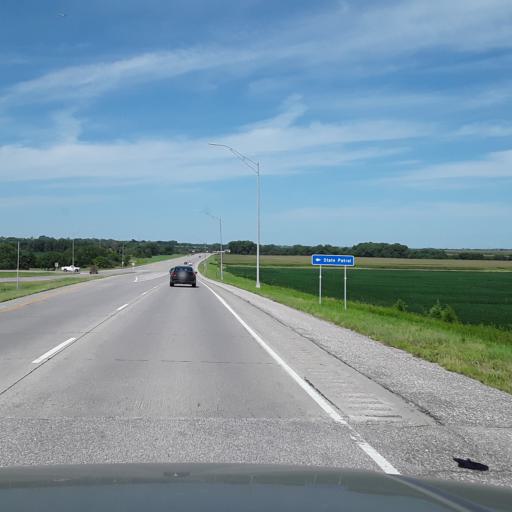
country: US
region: Nebraska
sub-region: Lancaster County
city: Lincoln
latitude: 40.8796
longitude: -96.7617
